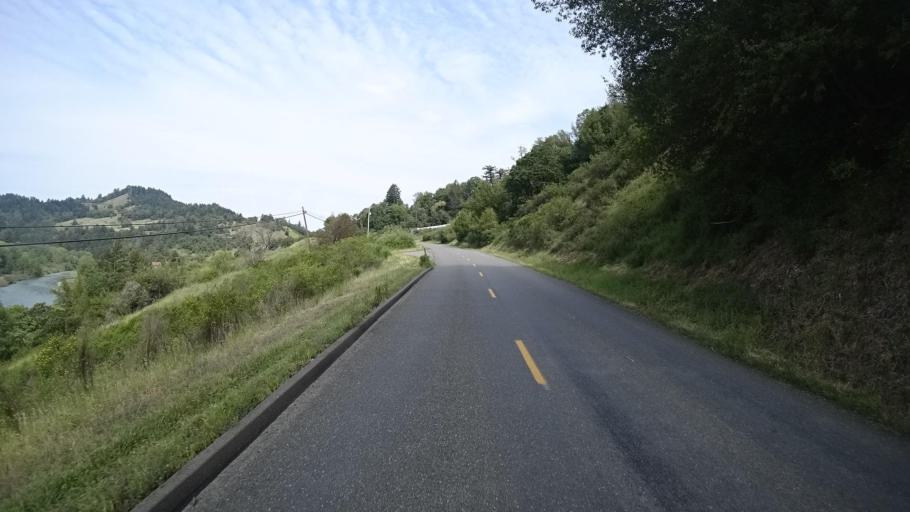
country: US
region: California
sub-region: Humboldt County
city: Redway
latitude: 40.0947
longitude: -123.7963
